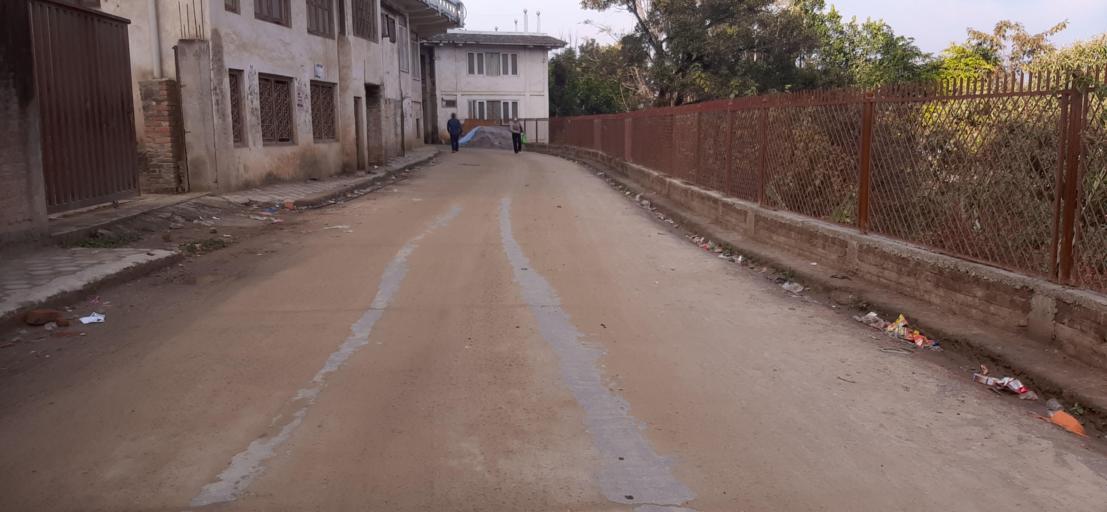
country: NP
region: Central Region
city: Kirtipur
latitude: 27.6747
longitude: 85.2816
